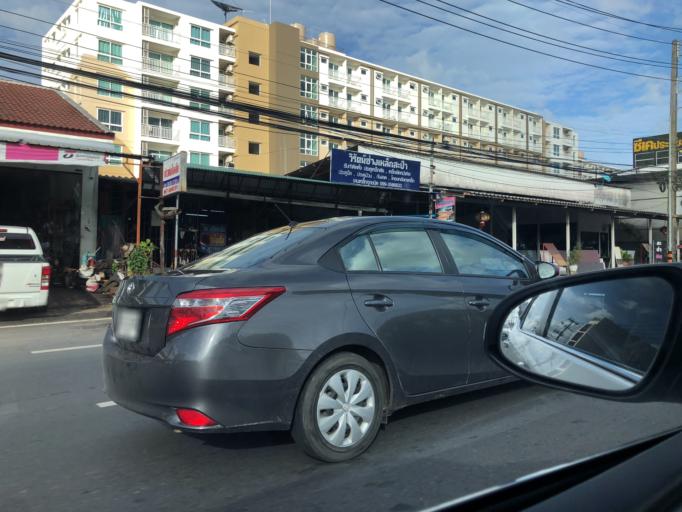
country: TH
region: Phuket
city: Ban Ko Kaeo
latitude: 7.9504
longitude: 98.3907
